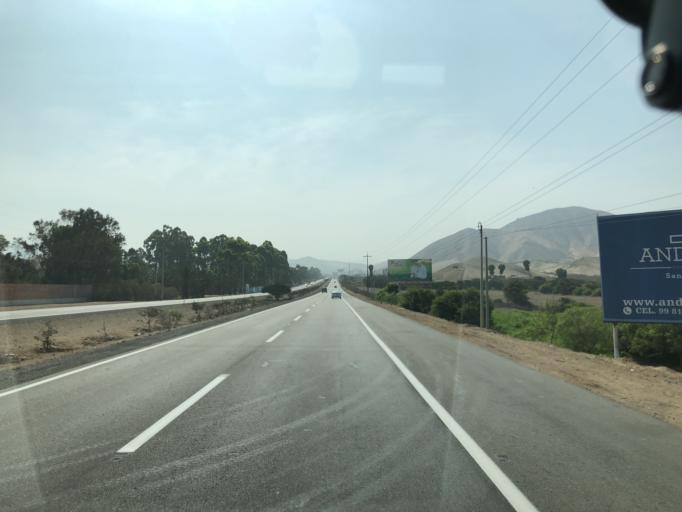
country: PE
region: Lima
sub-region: Provincia de Canete
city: Chilca
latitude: -12.5777
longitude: -76.6838
